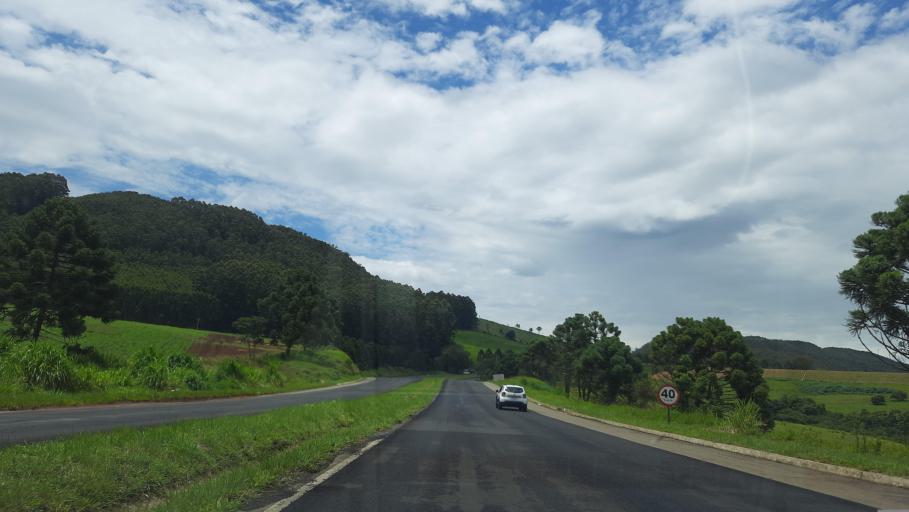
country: BR
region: Minas Gerais
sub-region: Pocos De Caldas
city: Pocos de Caldas
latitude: -21.8316
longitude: -46.6700
